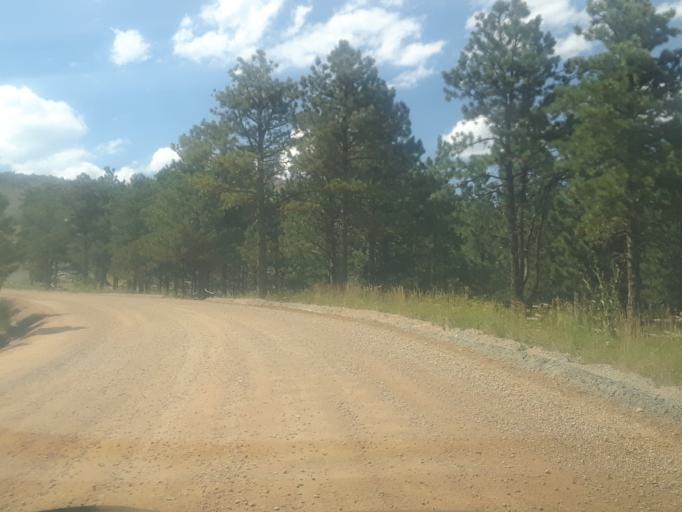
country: US
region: Colorado
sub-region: Boulder County
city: Boulder
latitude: 40.0614
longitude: -105.3737
